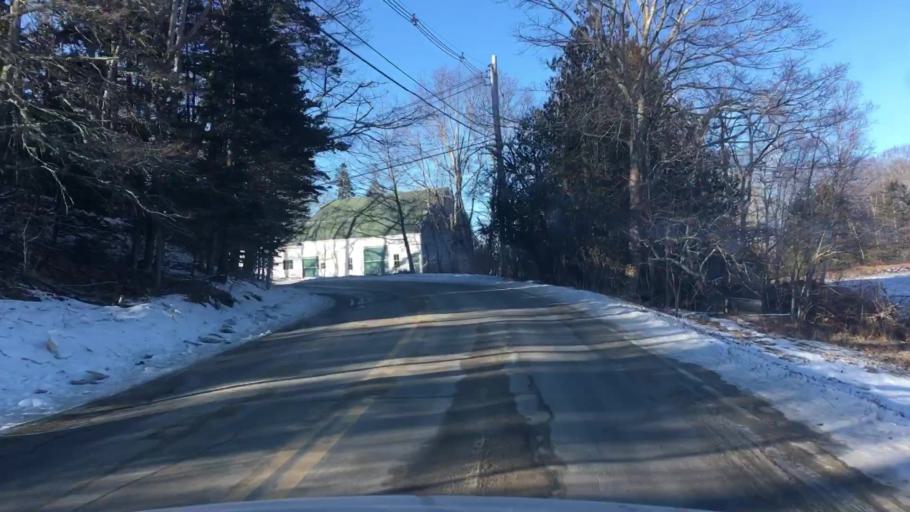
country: US
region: Maine
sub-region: Hancock County
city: Castine
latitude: 44.3485
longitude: -68.7476
